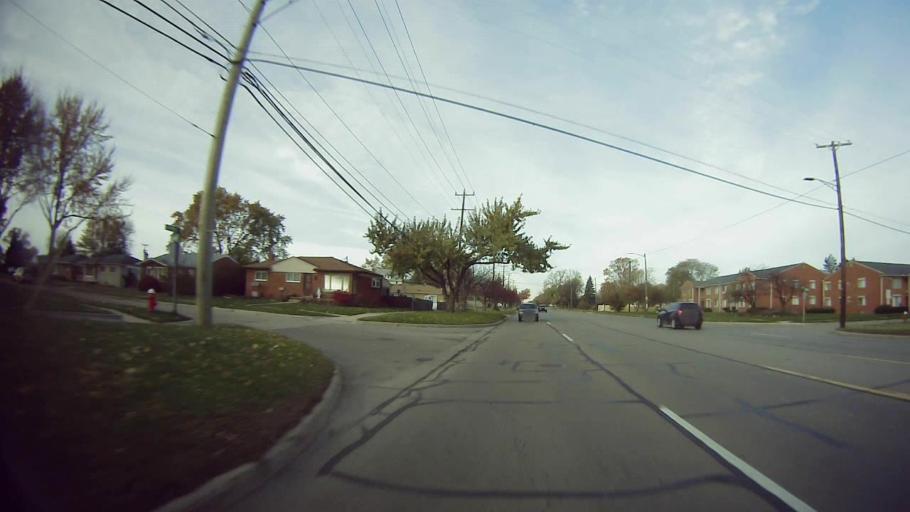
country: US
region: Michigan
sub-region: Macomb County
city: Warren
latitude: 42.4770
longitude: -83.0493
